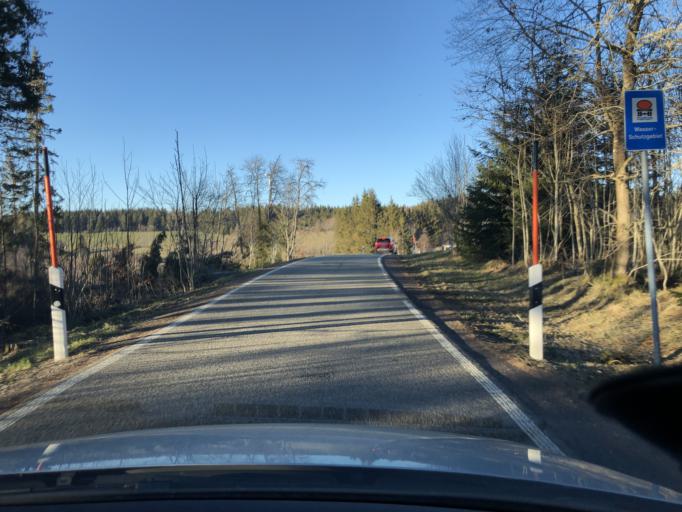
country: DE
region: Baden-Wuerttemberg
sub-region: Freiburg Region
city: Schluchsee
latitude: 47.8281
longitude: 8.2086
